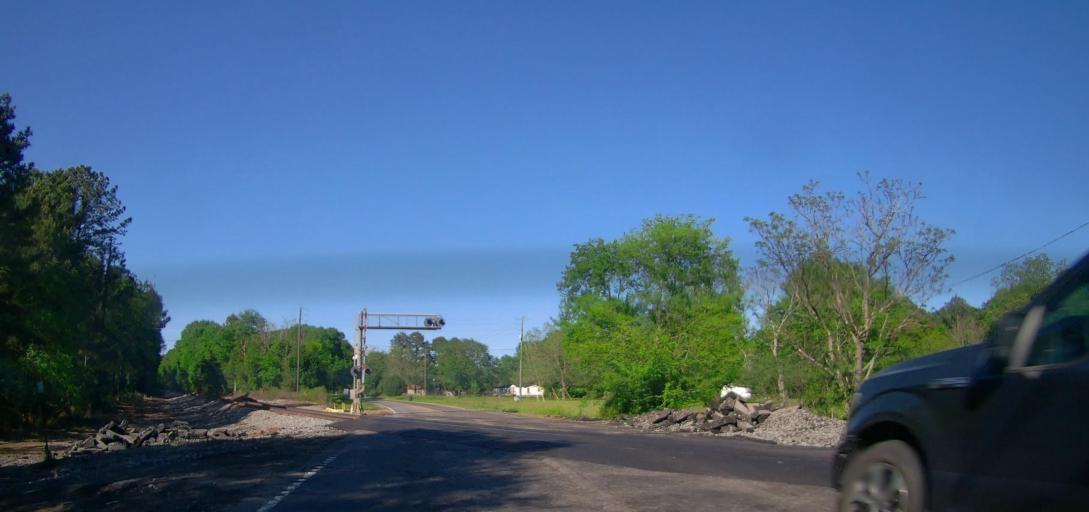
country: US
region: Georgia
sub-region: Houston County
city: Perry
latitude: 32.4546
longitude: -83.6204
